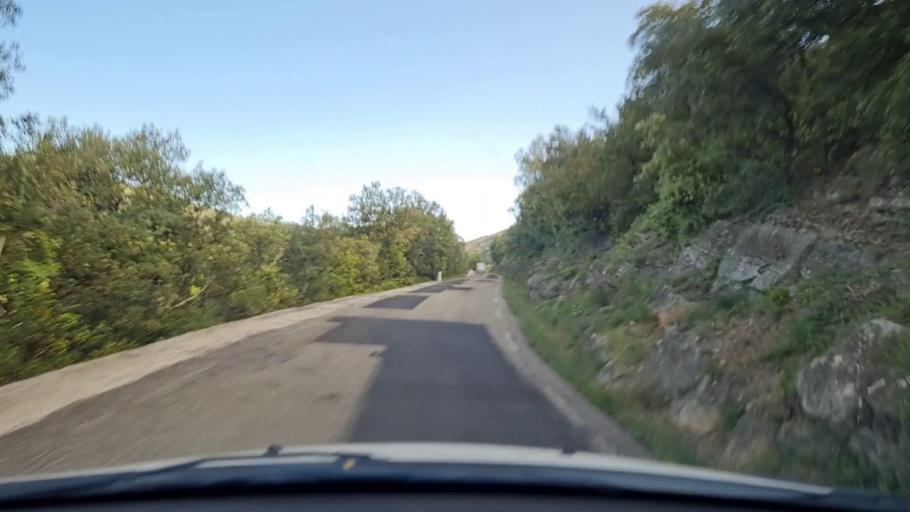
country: FR
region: Languedoc-Roussillon
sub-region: Departement du Gard
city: Les Salles-du-Gardon
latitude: 44.1793
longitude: 4.0202
